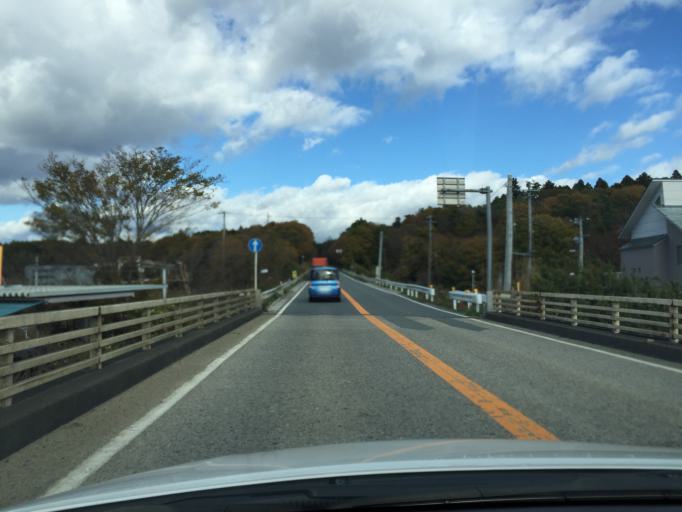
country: JP
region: Fukushima
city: Namie
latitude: 37.3888
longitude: 141.0079
